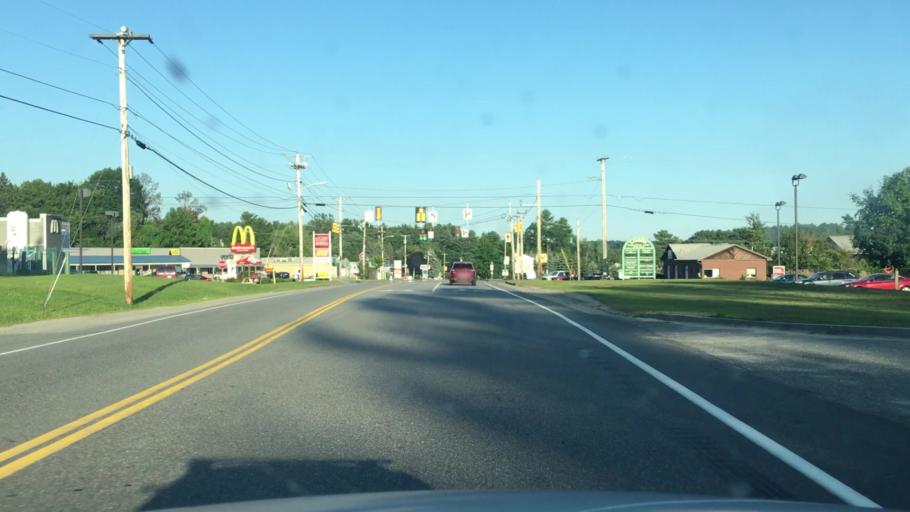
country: US
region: Maine
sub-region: Androscoggin County
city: Lisbon Falls
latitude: 44.0052
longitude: -70.0751
